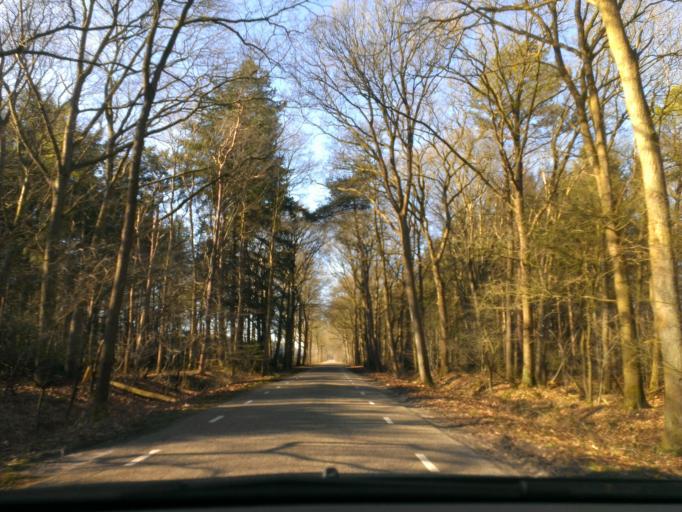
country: NL
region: Drenthe
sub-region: Gemeente Hoogeveen
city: Hoogeveen
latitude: 52.7202
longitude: 6.4124
